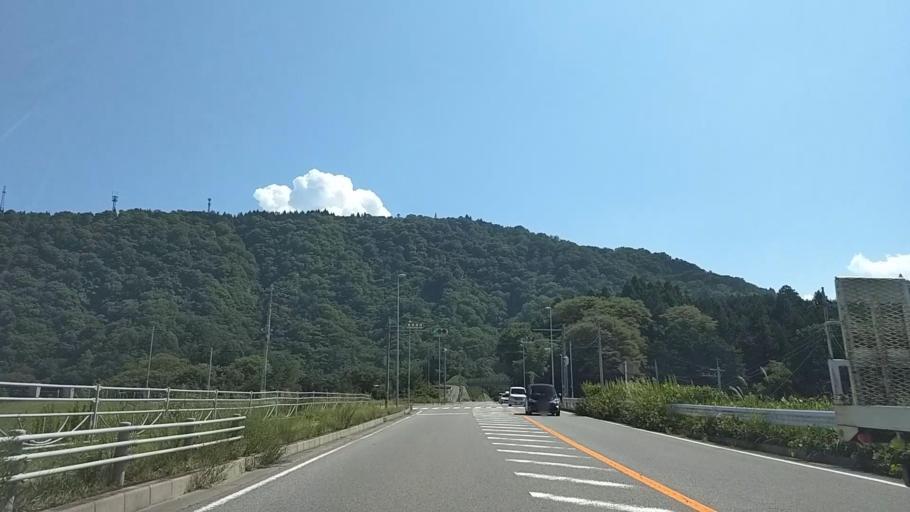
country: JP
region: Yamanashi
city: Ryuo
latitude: 35.5126
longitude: 138.4570
